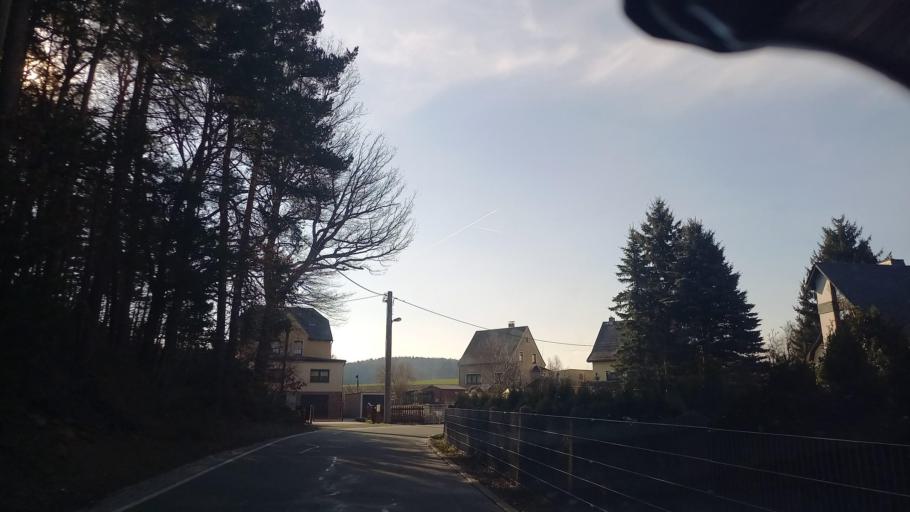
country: DE
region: Saxony
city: Kirchberg
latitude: 50.6031
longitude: 12.5232
